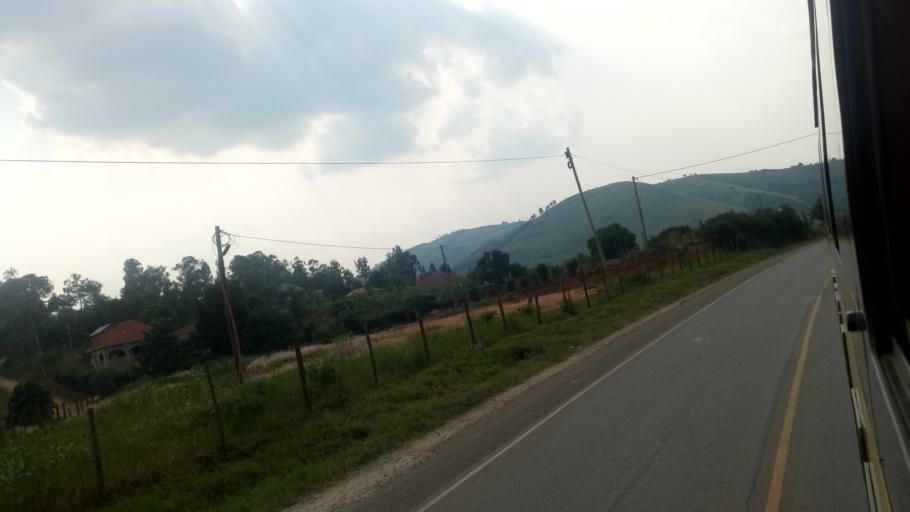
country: UG
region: Western Region
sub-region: Mbarara District
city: Mbarara
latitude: -0.5458
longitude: 30.7136
